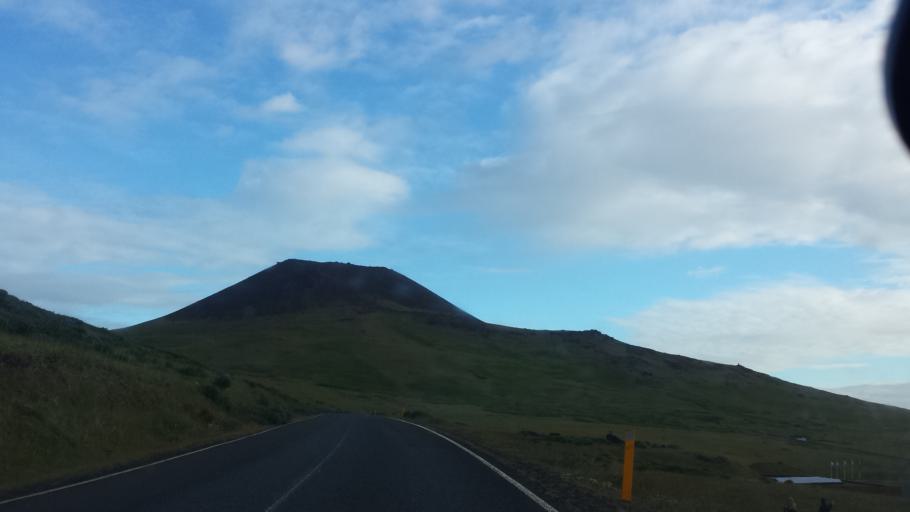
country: IS
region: South
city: Vestmannaeyjar
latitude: 63.4364
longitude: -20.2577
